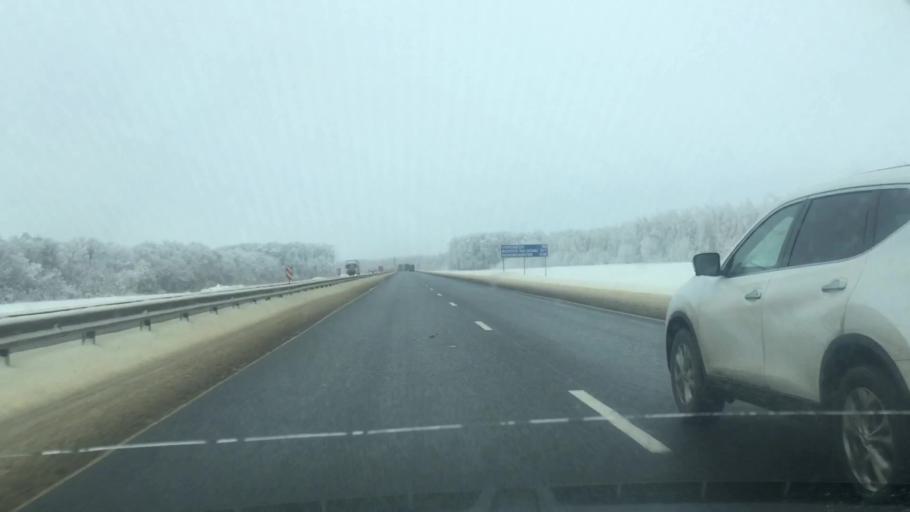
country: RU
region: Lipetsk
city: Zadonsk
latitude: 52.4973
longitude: 38.7559
